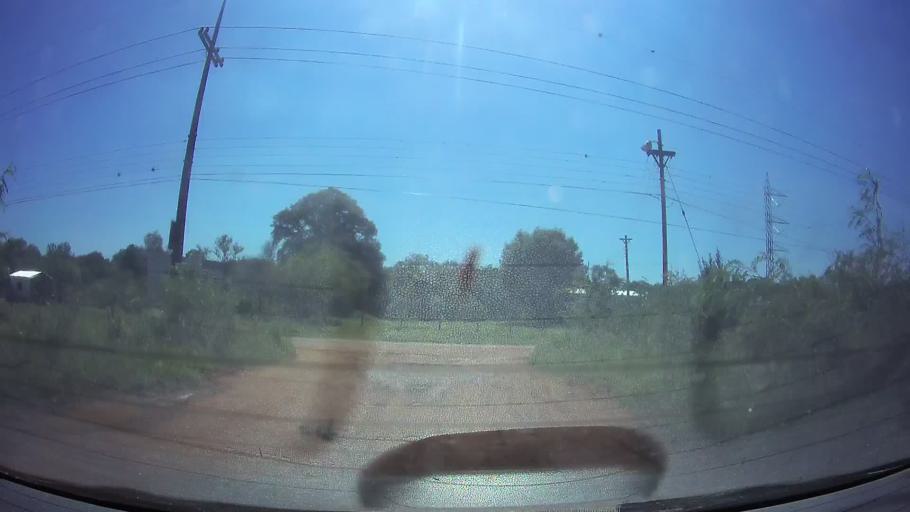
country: PY
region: Central
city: Limpio
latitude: -25.2370
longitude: -57.4402
